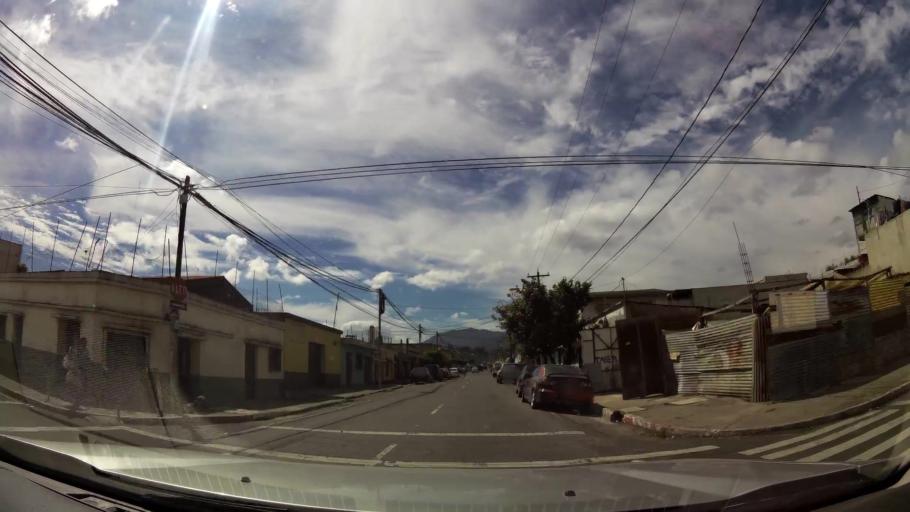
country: GT
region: Guatemala
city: Mixco
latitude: 14.6554
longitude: -90.5819
